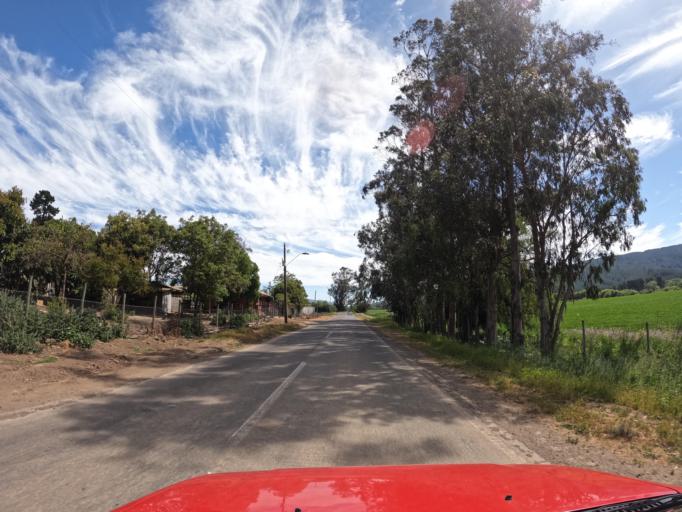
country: CL
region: Maule
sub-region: Provincia de Talca
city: Constitucion
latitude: -35.0060
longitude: -72.0304
